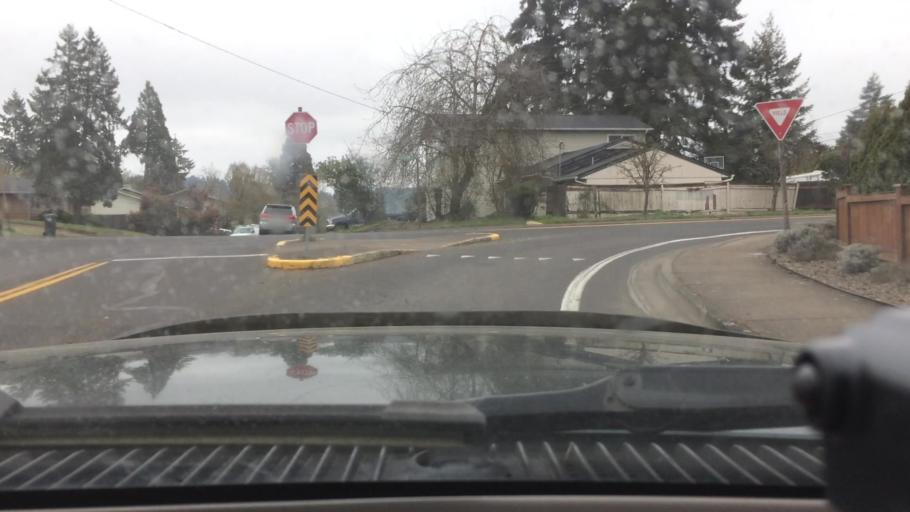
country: US
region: Oregon
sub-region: Lane County
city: Eugene
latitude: 44.0272
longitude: -123.1004
